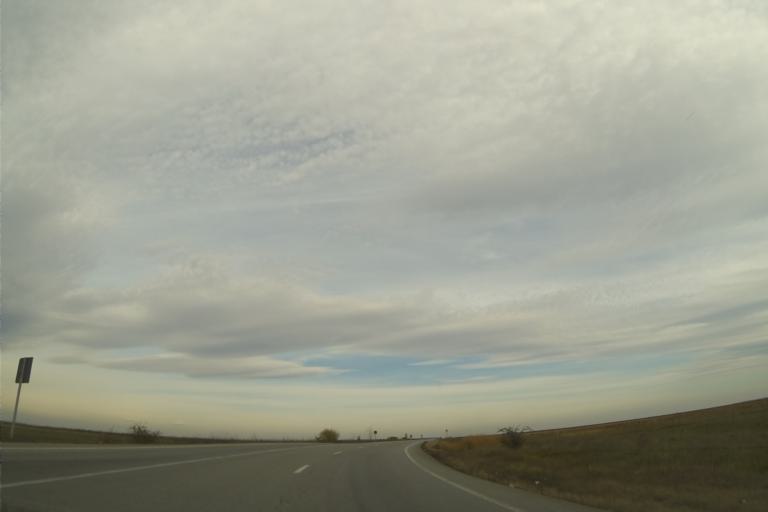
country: RO
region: Olt
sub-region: Comuna Valea Mare
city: Valea Mare
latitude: 44.4897
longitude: 24.4425
